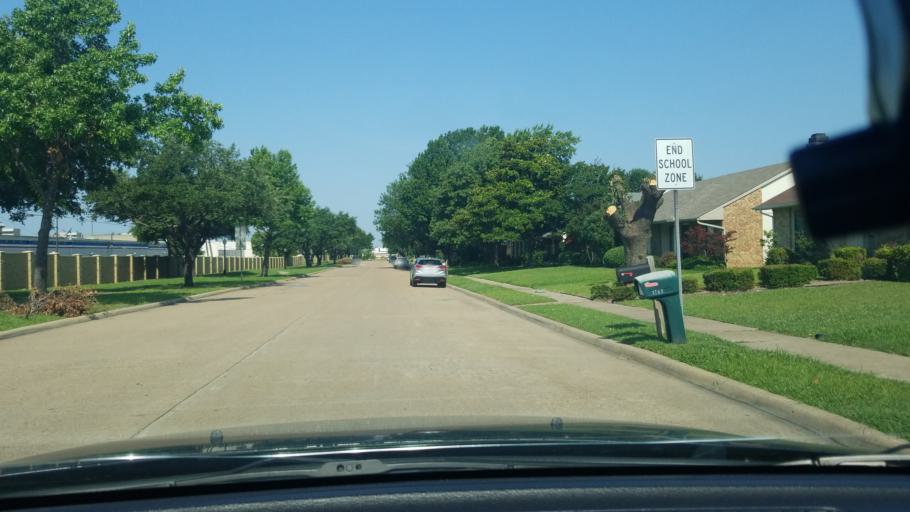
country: US
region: Texas
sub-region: Dallas County
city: Mesquite
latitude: 32.8166
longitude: -96.6232
